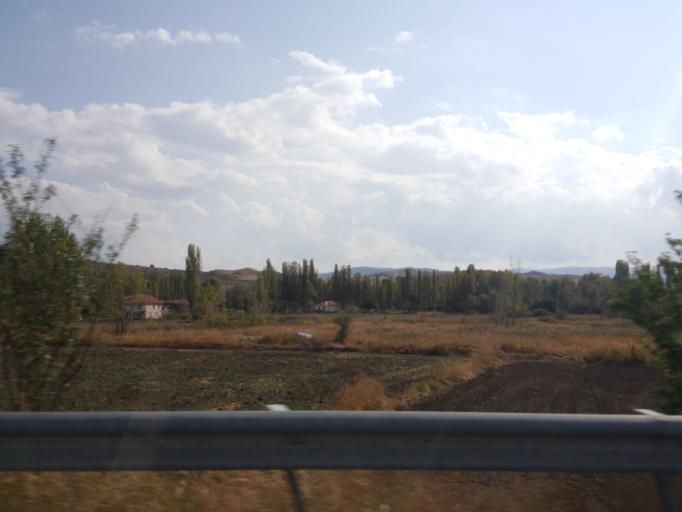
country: TR
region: Corum
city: Sungurlu
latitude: 40.1806
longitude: 34.4759
